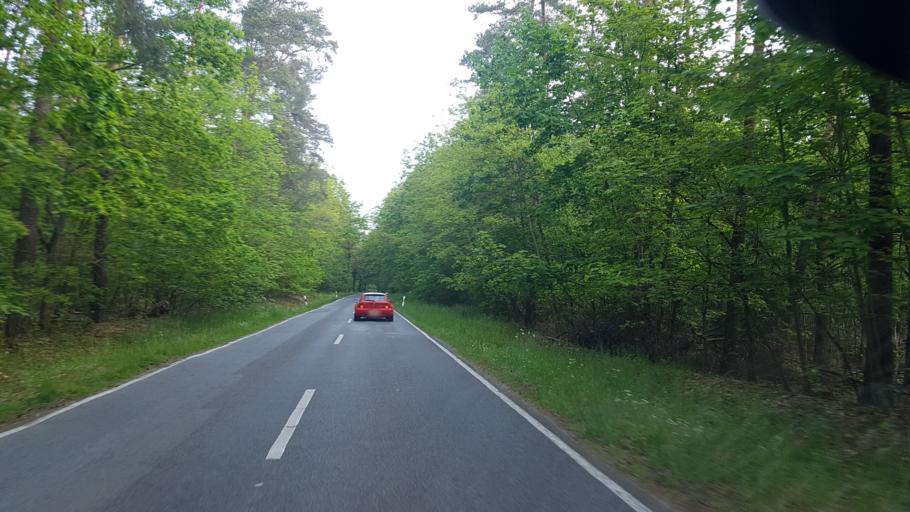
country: DE
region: Brandenburg
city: Baruth
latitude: 52.0159
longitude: 13.4701
